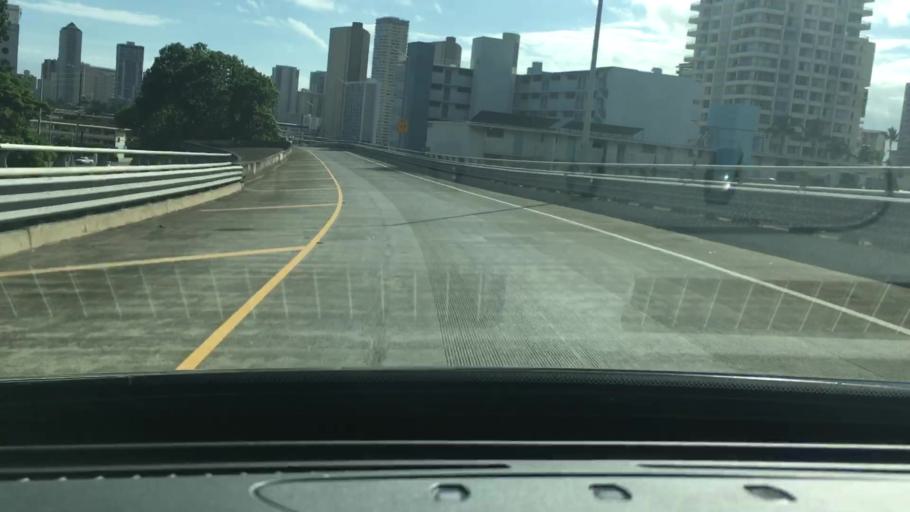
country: US
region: Hawaii
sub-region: Honolulu County
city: Honolulu
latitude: 21.2894
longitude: -157.8166
